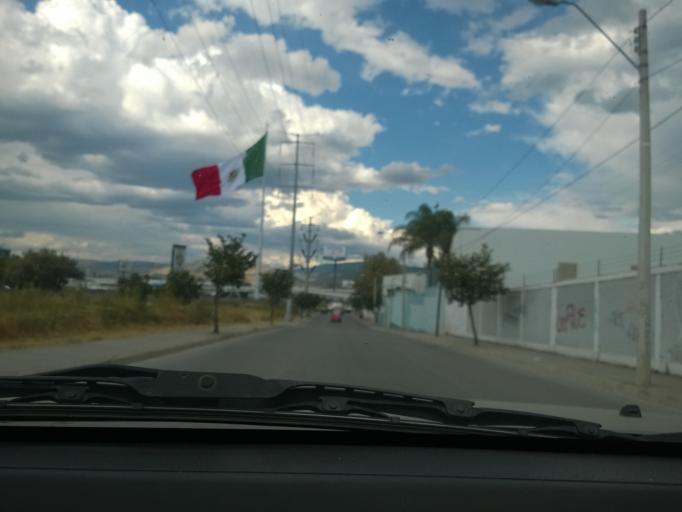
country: MX
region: Guanajuato
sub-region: Leon
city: Fraccionamiento Paraiso Real
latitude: 21.0931
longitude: -101.6290
